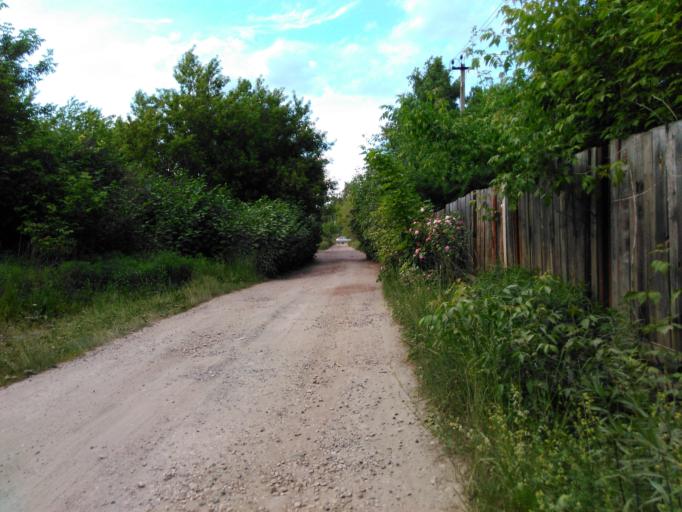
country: RU
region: Moskovskaya
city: Vishnyakovskiye Dachi
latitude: 55.7615
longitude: 38.1420
